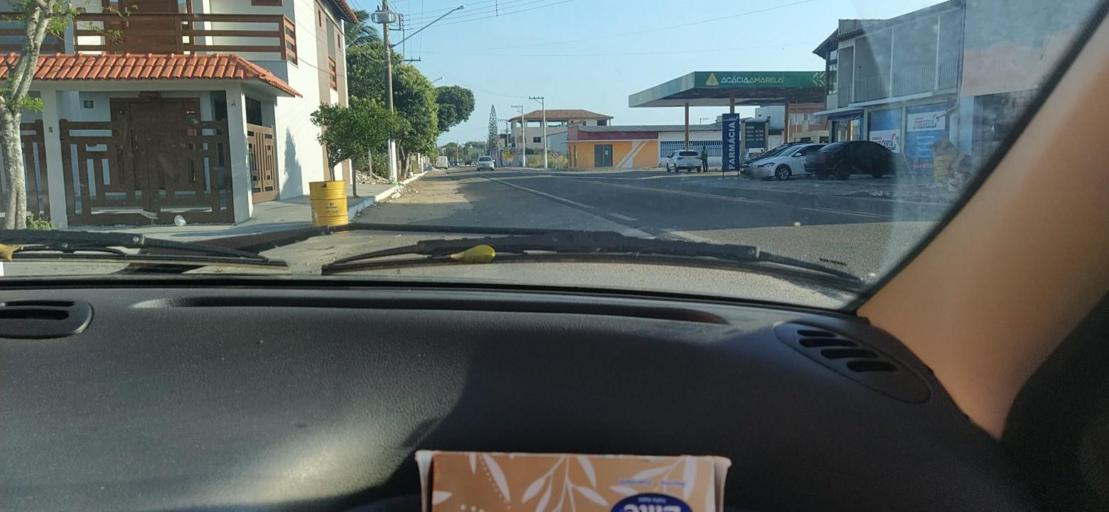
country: BR
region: Espirito Santo
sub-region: Conceicao Da Barra
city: Conceicao da Barra
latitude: -18.5801
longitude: -39.7329
